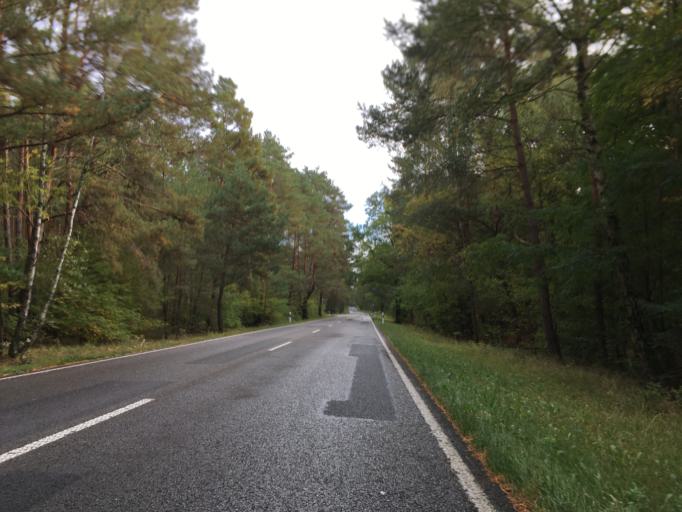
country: DE
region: Brandenburg
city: Oderberg
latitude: 52.8869
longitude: 14.1089
